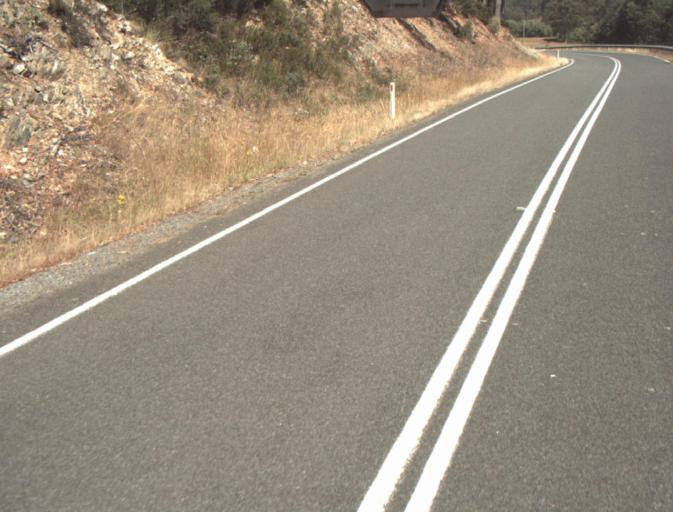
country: AU
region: Tasmania
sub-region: Dorset
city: Scottsdale
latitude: -41.2992
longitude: 147.3836
